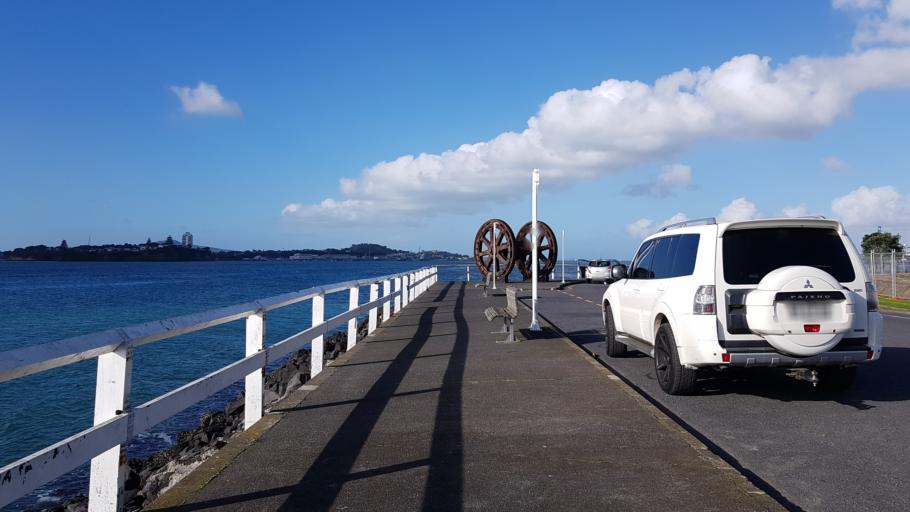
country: NZ
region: Auckland
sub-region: Auckland
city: Auckland
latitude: -36.8365
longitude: 174.7587
